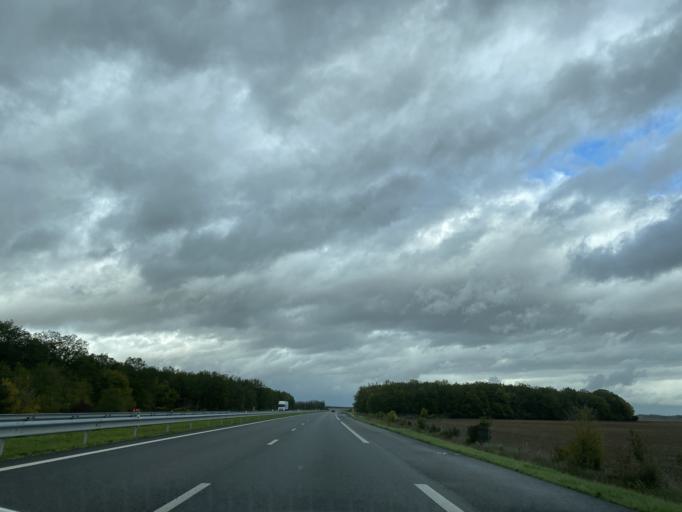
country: FR
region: Centre
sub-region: Departement du Cher
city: Levet
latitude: 46.8863
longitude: 2.4194
